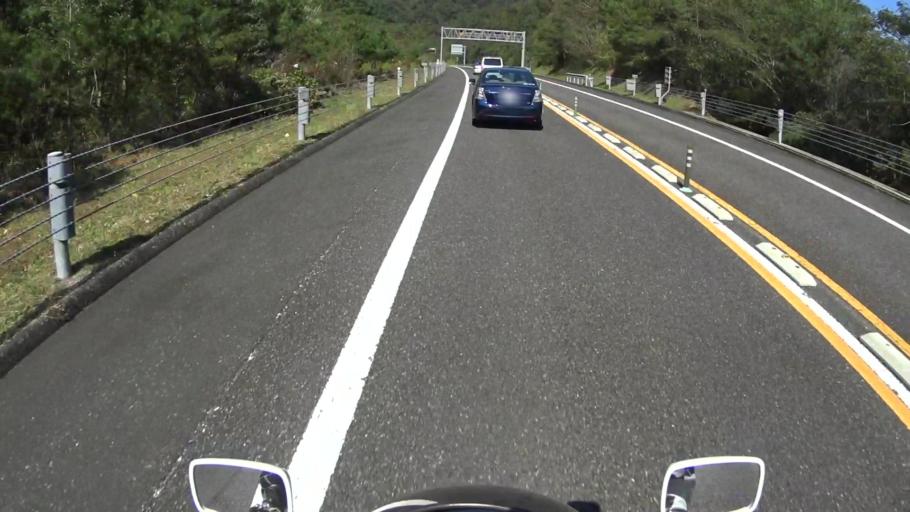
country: JP
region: Kyoto
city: Ayabe
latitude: 35.3635
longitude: 135.2881
